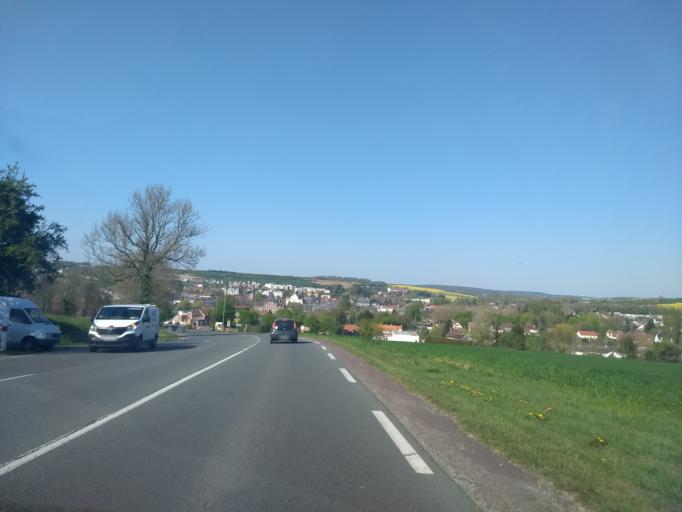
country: FR
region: Picardie
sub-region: Departement de la Somme
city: Doullens
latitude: 50.1495
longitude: 2.3391
